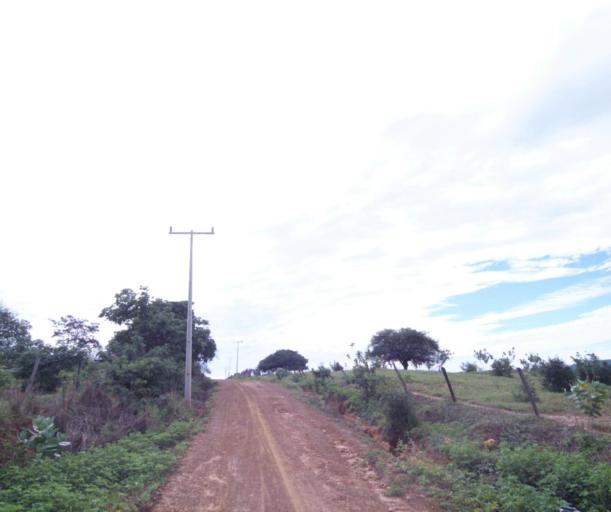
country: BR
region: Bahia
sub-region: Carinhanha
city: Carinhanha
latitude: -14.2403
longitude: -44.3917
